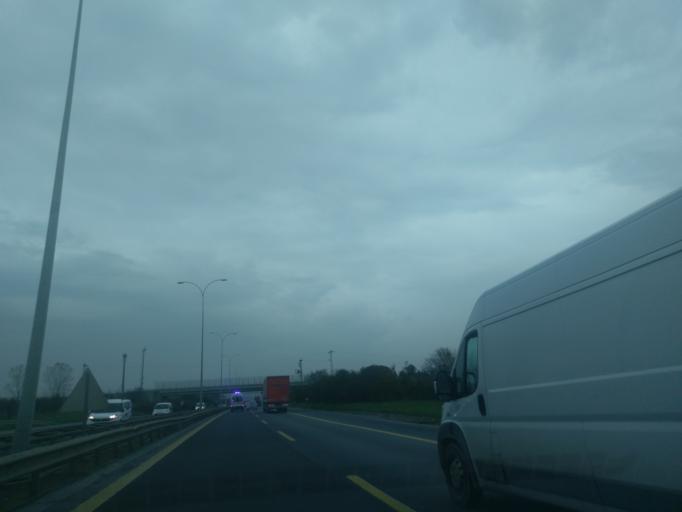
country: TR
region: Istanbul
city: Muratbey
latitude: 41.1066
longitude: 28.5440
